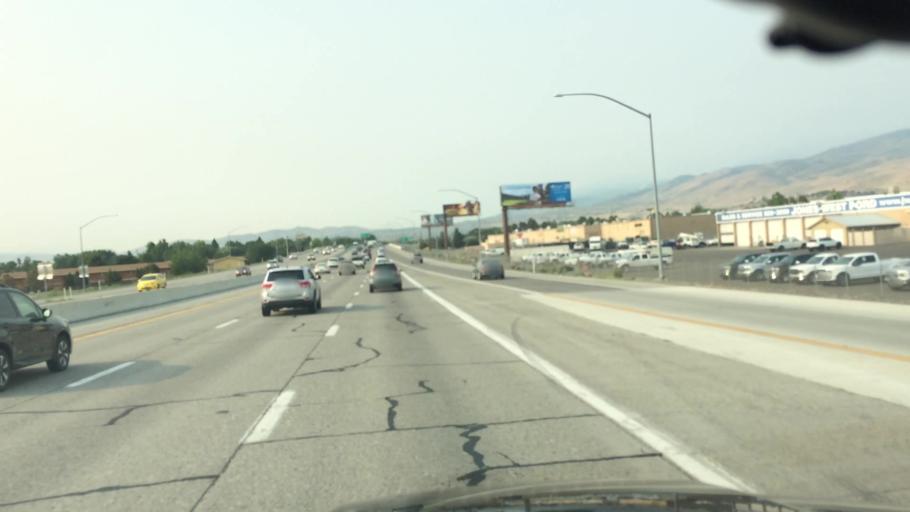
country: US
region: Nevada
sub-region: Washoe County
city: Reno
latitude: 39.4906
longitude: -119.7852
